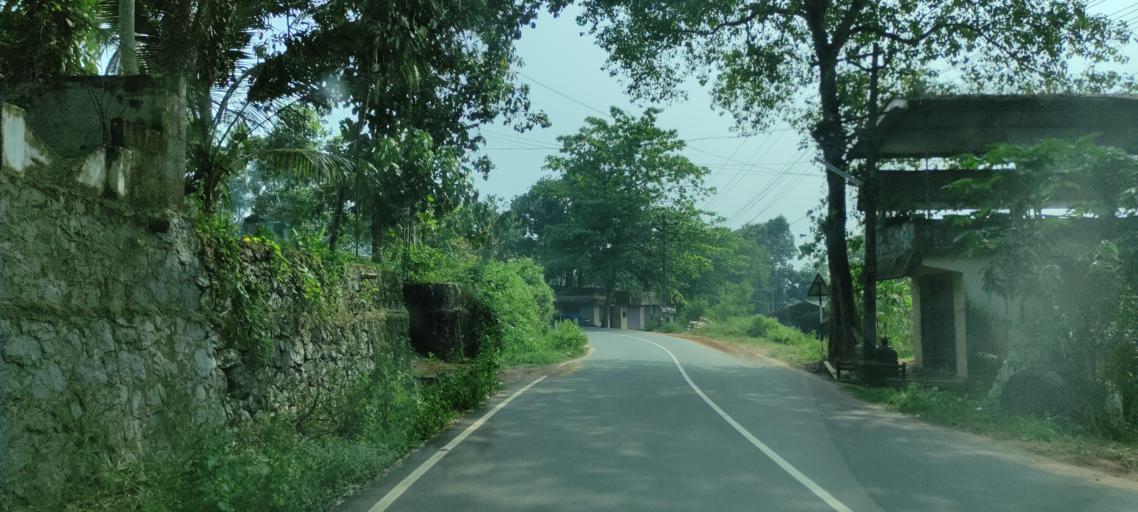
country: IN
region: Kerala
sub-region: Pattanamtitta
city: Adur
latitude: 9.2424
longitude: 76.6814
